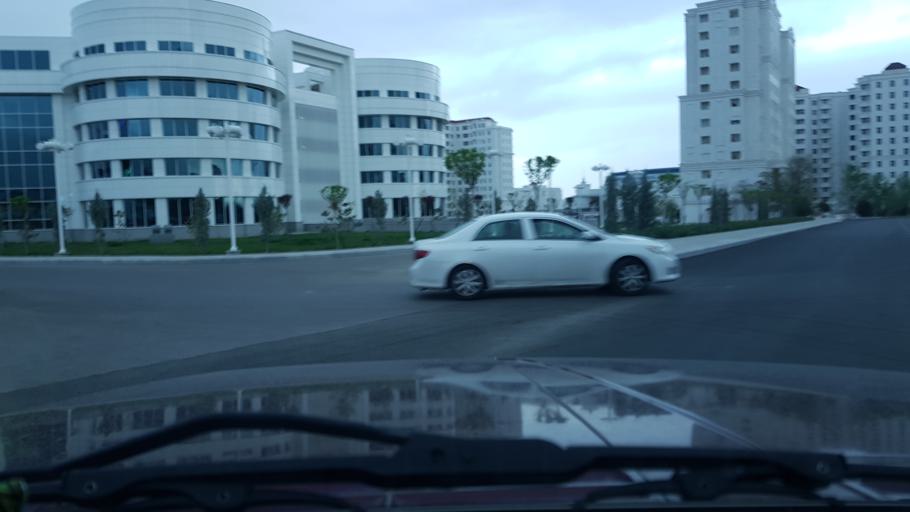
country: TM
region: Ahal
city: Ashgabat
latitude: 37.8914
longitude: 58.3762
